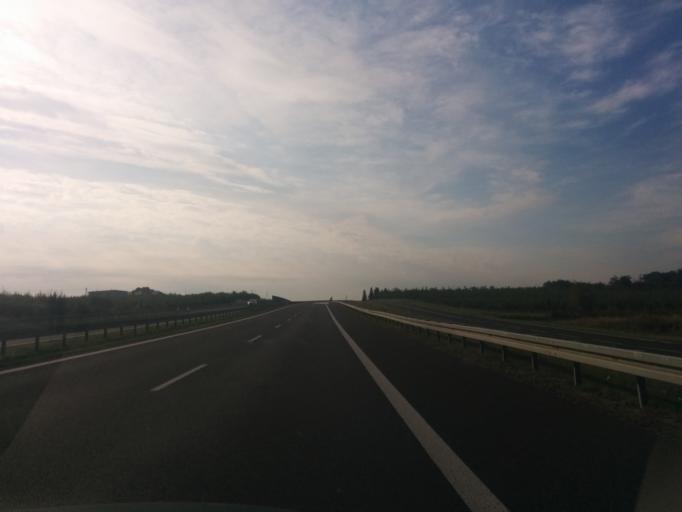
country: PL
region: Masovian Voivodeship
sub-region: Powiat grojecki
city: Jasieniec
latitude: 51.7941
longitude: 20.8912
